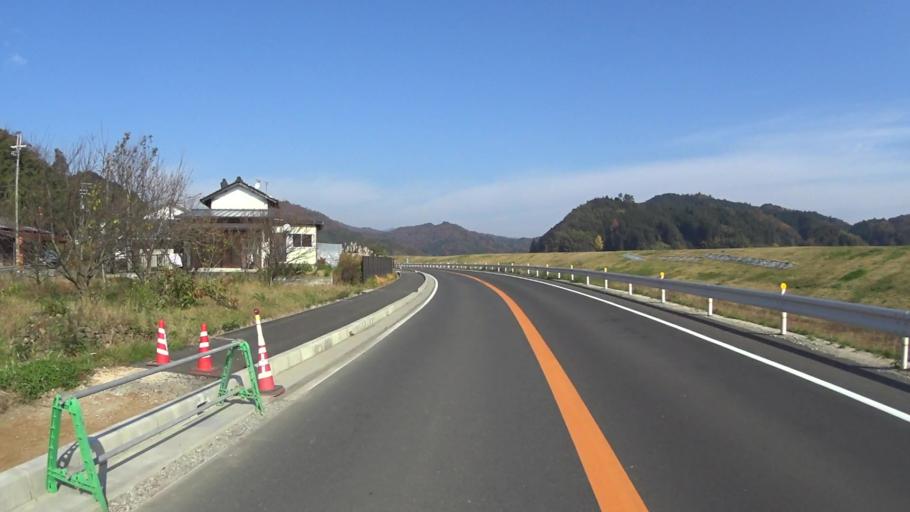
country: JP
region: Kyoto
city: Fukuchiyama
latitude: 35.3971
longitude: 135.1823
